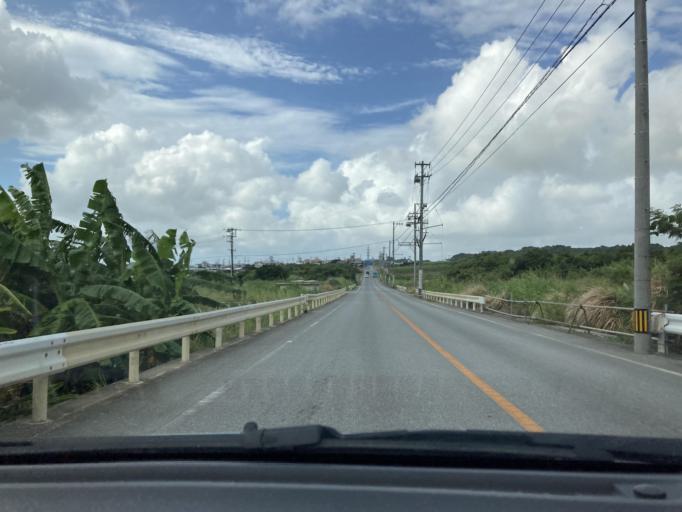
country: JP
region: Okinawa
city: Itoman
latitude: 26.0990
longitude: 127.6985
